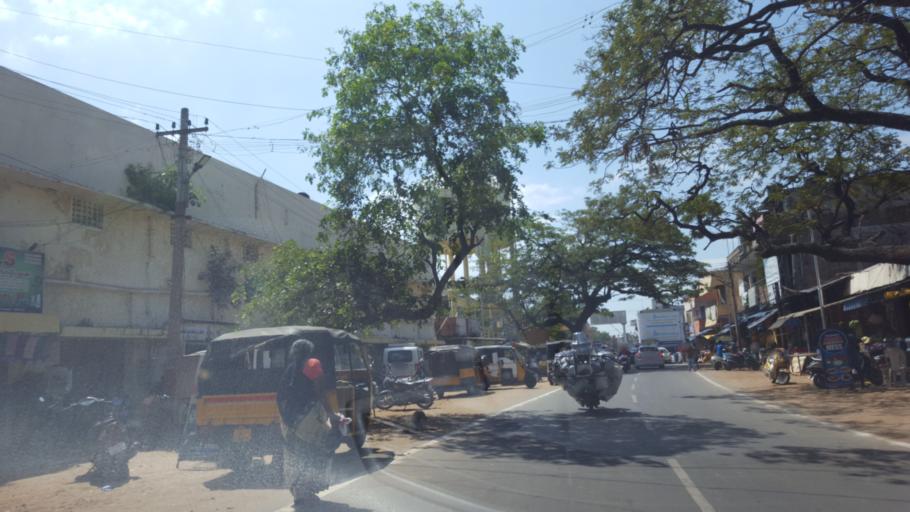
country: IN
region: Tamil Nadu
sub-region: Kancheepuram
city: Mamallapuram
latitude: 12.6216
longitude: 80.1945
